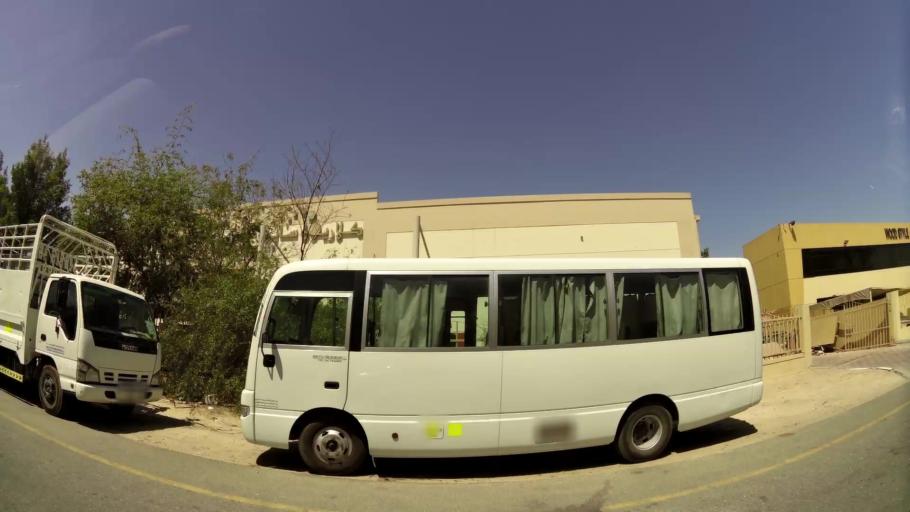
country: AE
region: Dubai
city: Dubai
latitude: 24.9795
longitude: 55.2061
